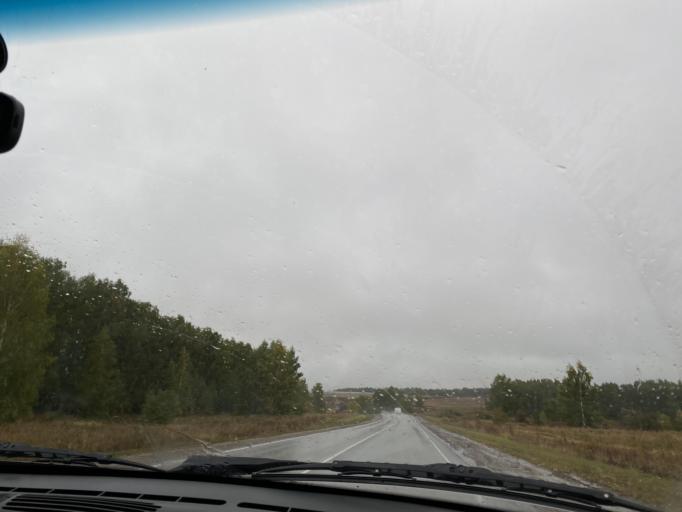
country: RU
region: Rjazan
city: Murmino
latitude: 54.4637
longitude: 39.8673
